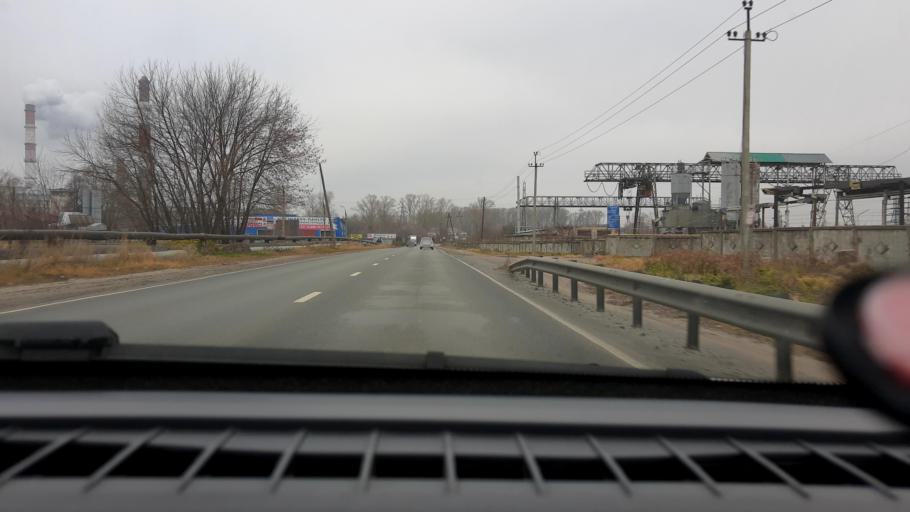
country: RU
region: Nizjnij Novgorod
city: Novaya Balakhna
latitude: 56.4959
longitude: 43.5945
